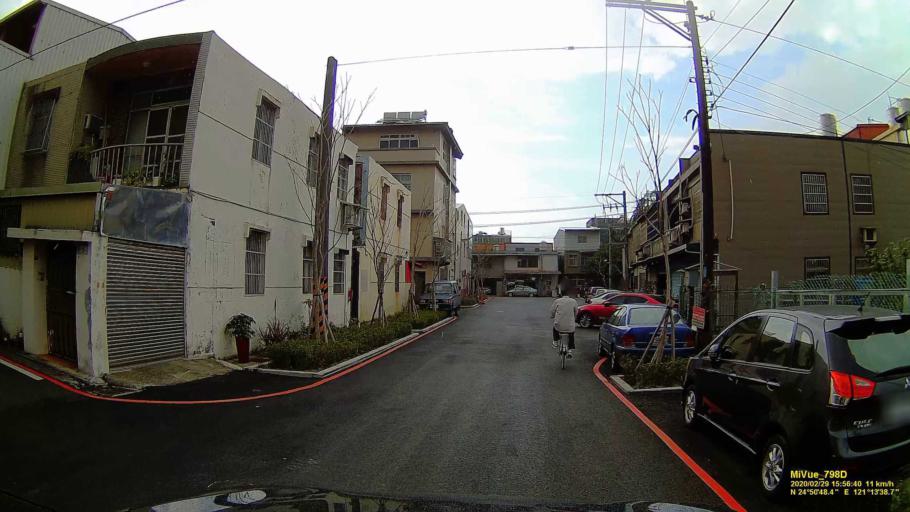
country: TW
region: Taiwan
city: Daxi
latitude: 24.8468
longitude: 121.2274
